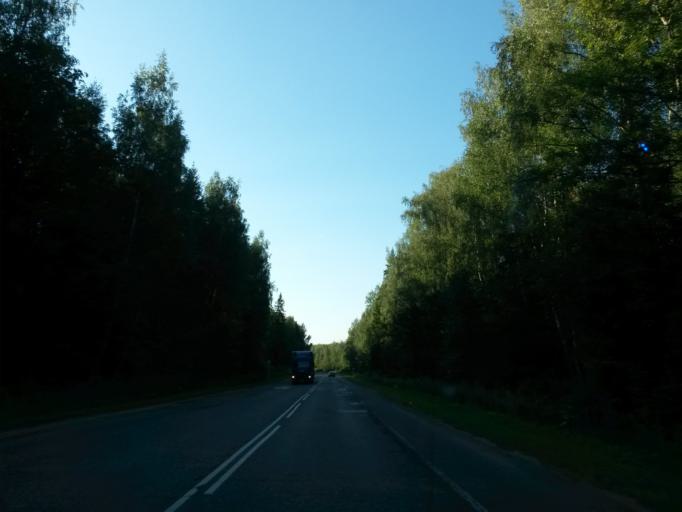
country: RU
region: Ivanovo
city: Pistsovo
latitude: 57.1121
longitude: 40.6485
